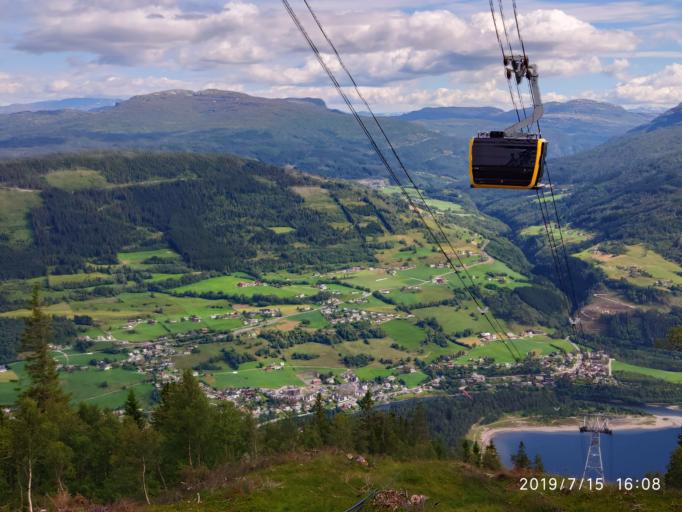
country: NO
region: Hordaland
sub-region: Voss
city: Voss
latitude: 60.6430
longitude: 6.4037
